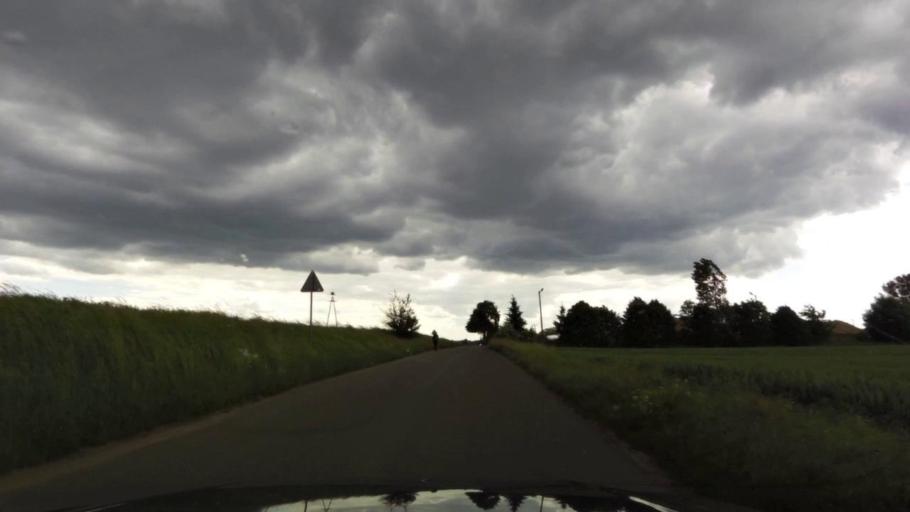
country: PL
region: West Pomeranian Voivodeship
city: Trzcinsko Zdroj
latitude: 52.9566
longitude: 14.6092
